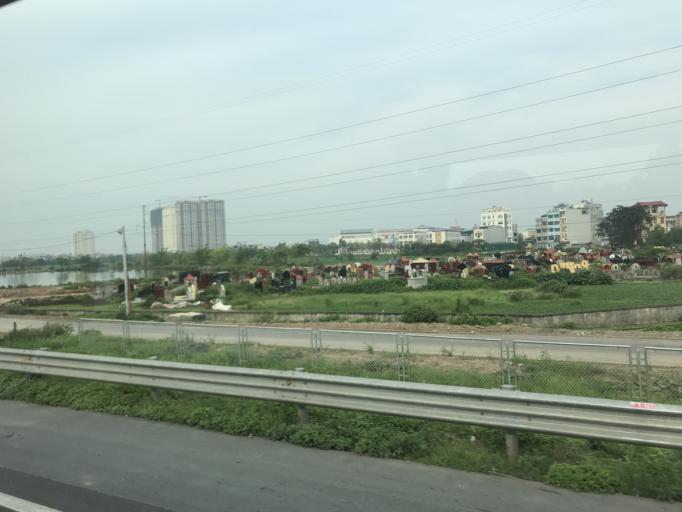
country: VN
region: Ha Noi
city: Van Dien
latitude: 20.9393
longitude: 105.8593
